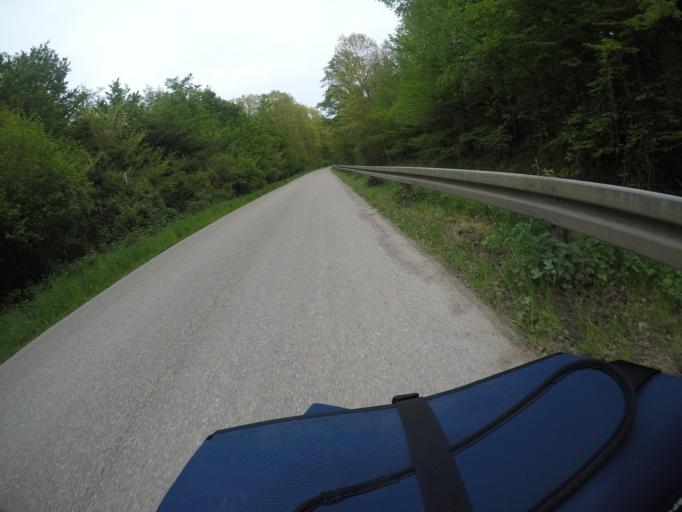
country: DE
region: Baden-Wuerttemberg
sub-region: Freiburg Region
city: Offenburg
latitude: 48.4745
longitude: 7.9096
